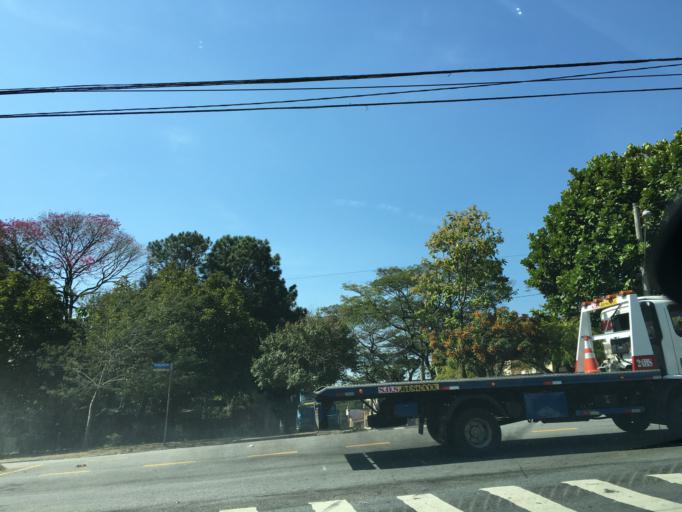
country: BR
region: Sao Paulo
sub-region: Osasco
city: Osasco
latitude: -23.5759
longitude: -46.7257
